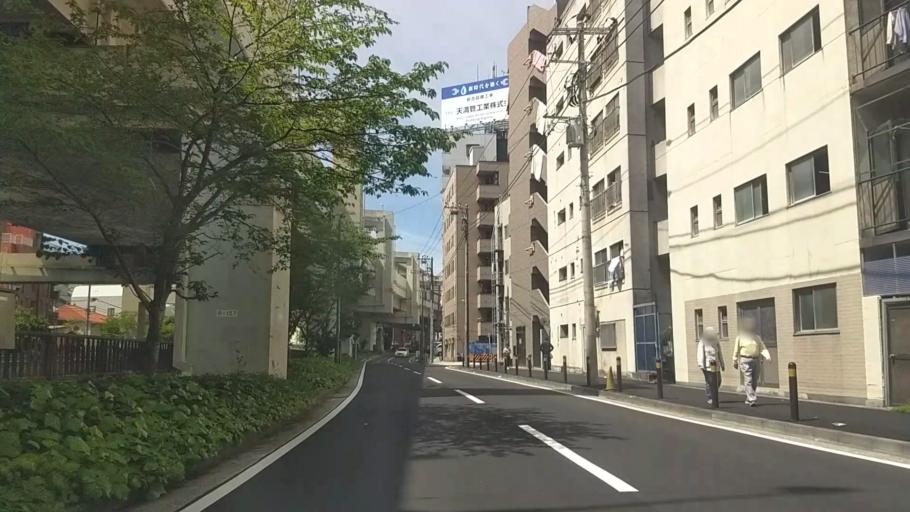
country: JP
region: Kanagawa
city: Yokohama
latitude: 35.4380
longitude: 139.6401
